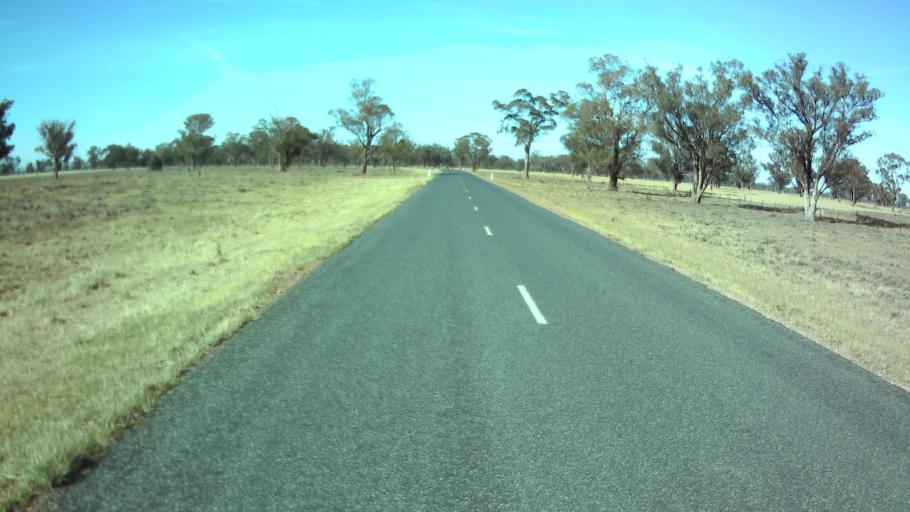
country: AU
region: New South Wales
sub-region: Weddin
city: Grenfell
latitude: -34.0569
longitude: 147.9132
